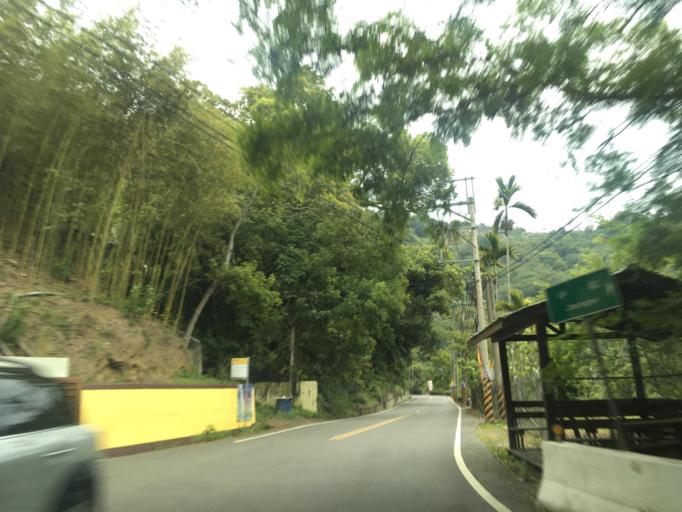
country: TW
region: Taiwan
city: Fengyuan
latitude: 24.1657
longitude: 120.8246
